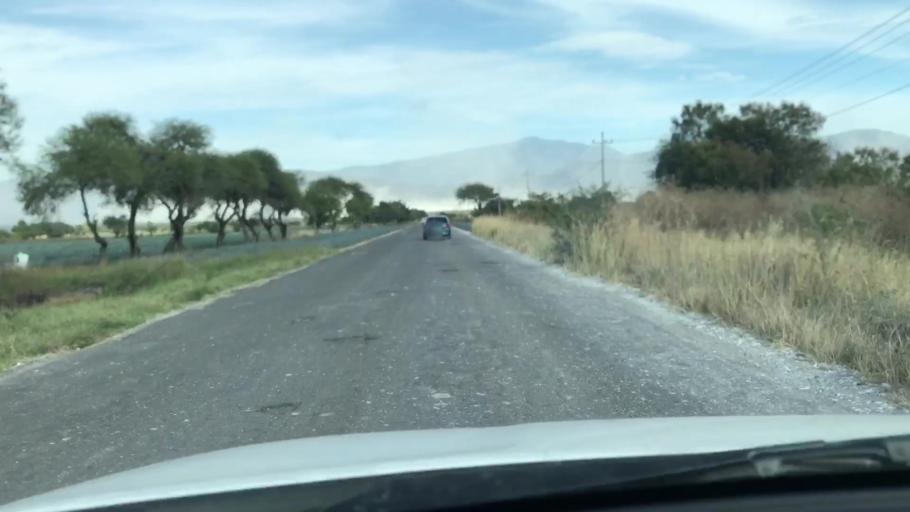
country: MX
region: Jalisco
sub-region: Zacoalco de Torres
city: Barranca de Otates (Barranca de Otatan)
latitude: 20.2810
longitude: -103.6212
